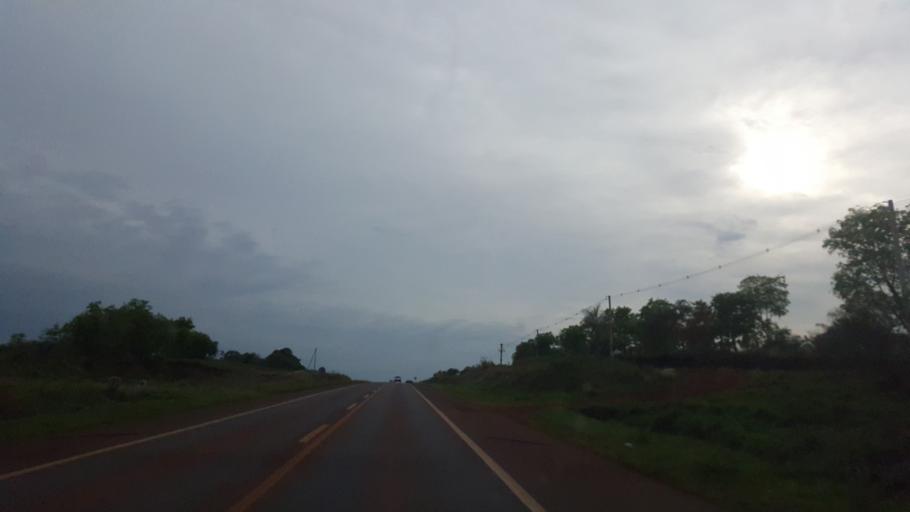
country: AR
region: Misiones
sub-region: Departamento de Apostoles
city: San Jose
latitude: -27.7623
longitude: -55.7940
